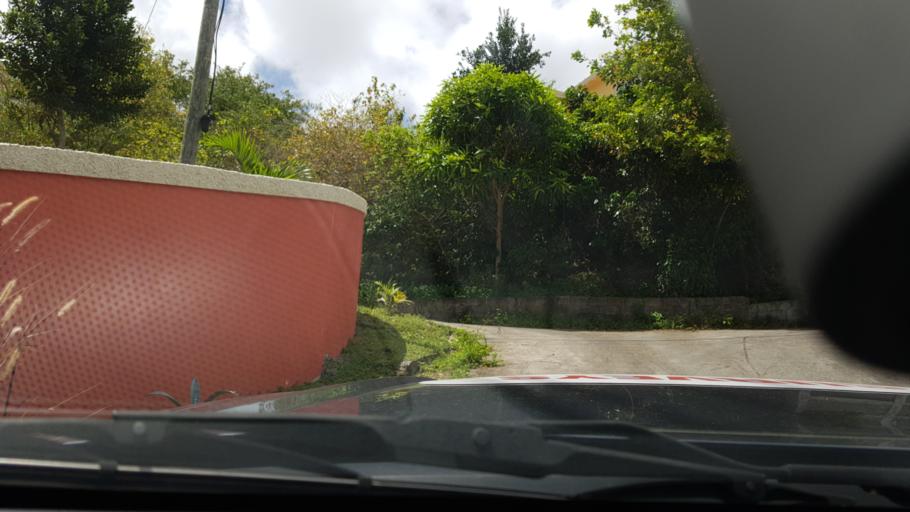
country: LC
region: Gros-Islet
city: Gros Islet
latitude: 14.0655
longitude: -60.9291
